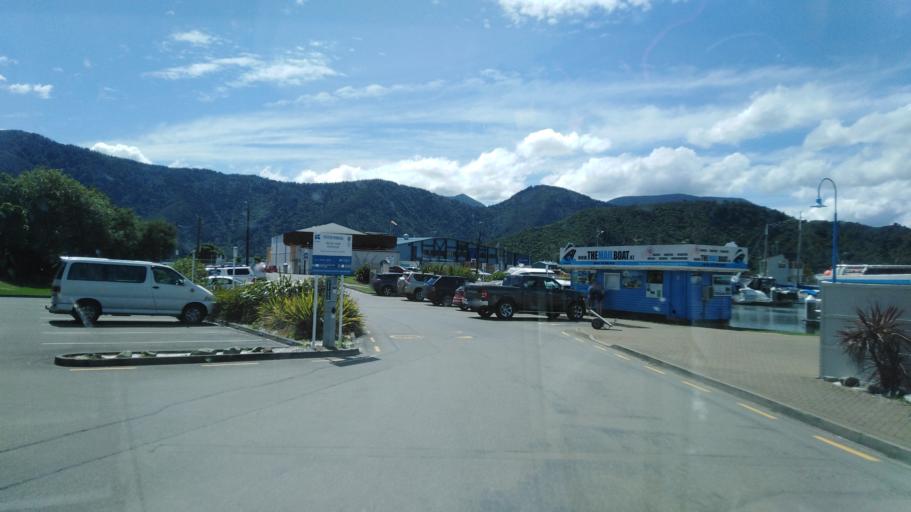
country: NZ
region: Marlborough
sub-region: Marlborough District
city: Picton
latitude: -41.2760
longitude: 173.7688
